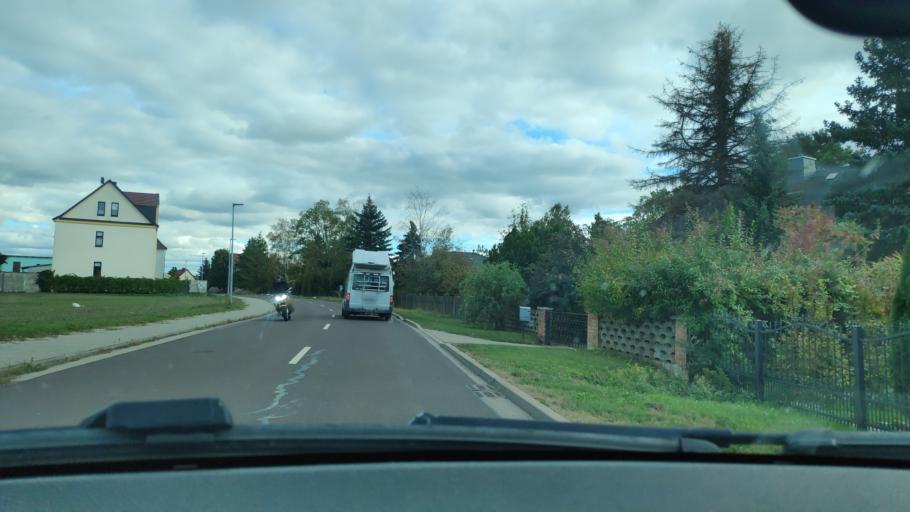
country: DE
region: Saxony-Anhalt
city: Biederitz
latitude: 52.1570
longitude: 11.7229
